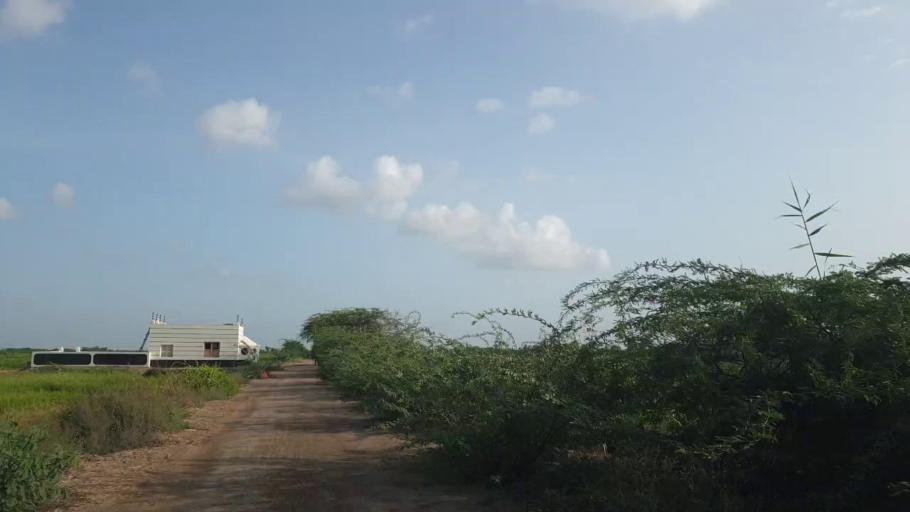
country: PK
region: Sindh
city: Kadhan
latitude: 24.6374
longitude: 69.1051
